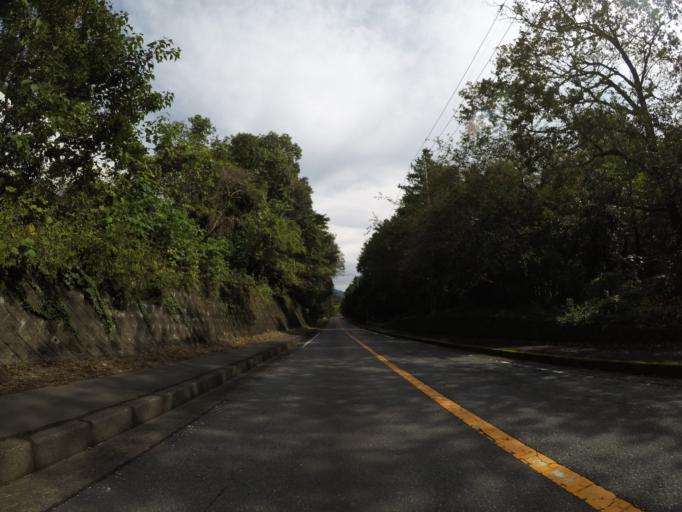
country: JP
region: Shizuoka
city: Fuji
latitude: 35.1953
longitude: 138.6934
